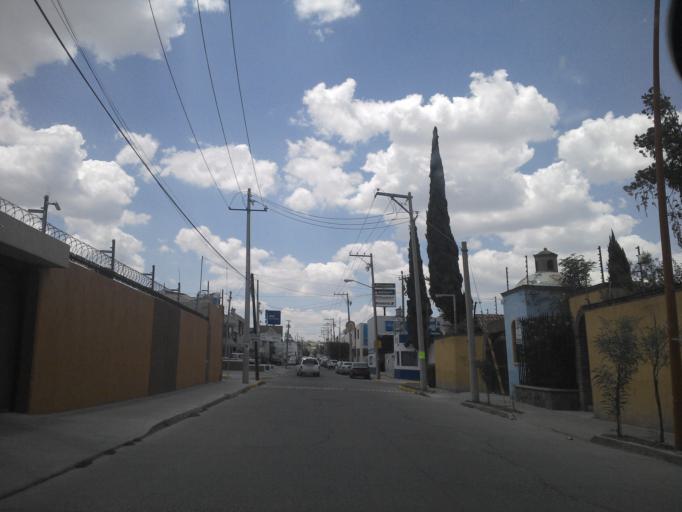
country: MX
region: Guanajuato
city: San Francisco del Rincon
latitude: 21.0269
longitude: -101.8577
